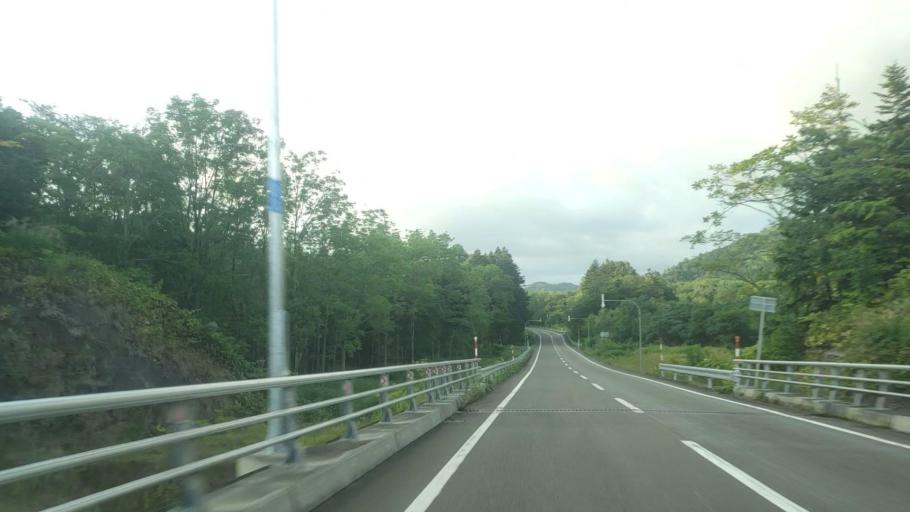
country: JP
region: Hokkaido
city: Bibai
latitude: 43.1103
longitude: 142.0989
